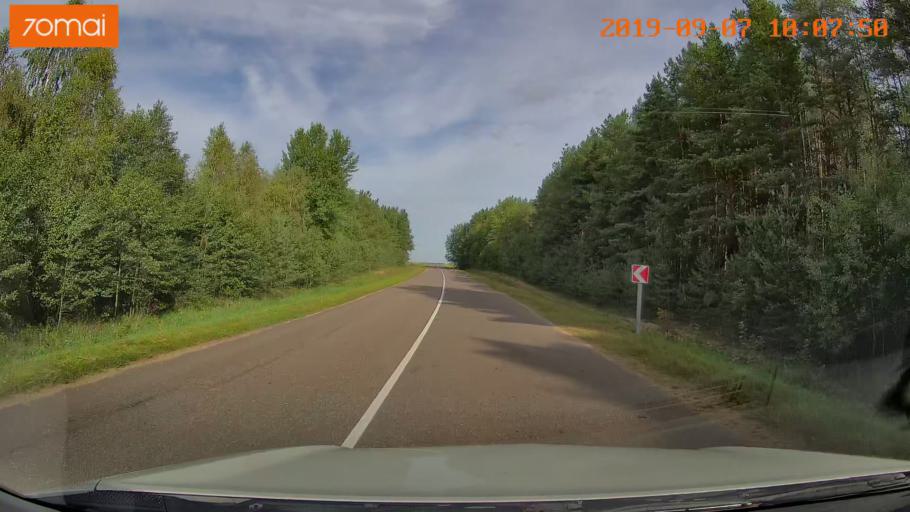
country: BY
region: Grodnenskaya
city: Voranava
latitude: 54.0807
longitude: 25.3950
